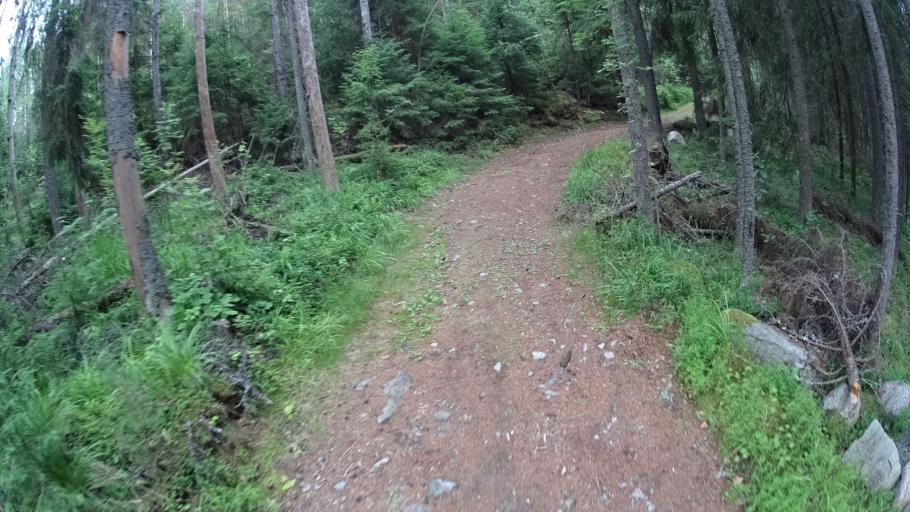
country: FI
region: Southern Savonia
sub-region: Mikkeli
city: Maentyharju
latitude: 61.1764
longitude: 26.8968
